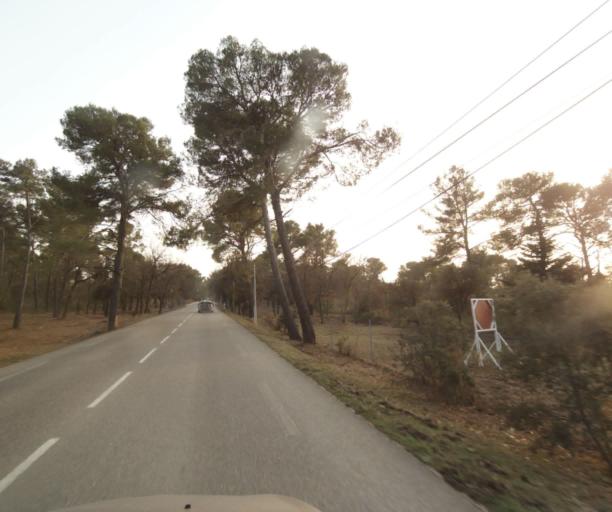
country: FR
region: Provence-Alpes-Cote d'Azur
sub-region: Departement des Bouches-du-Rhone
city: Rognes
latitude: 43.6363
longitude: 5.3610
